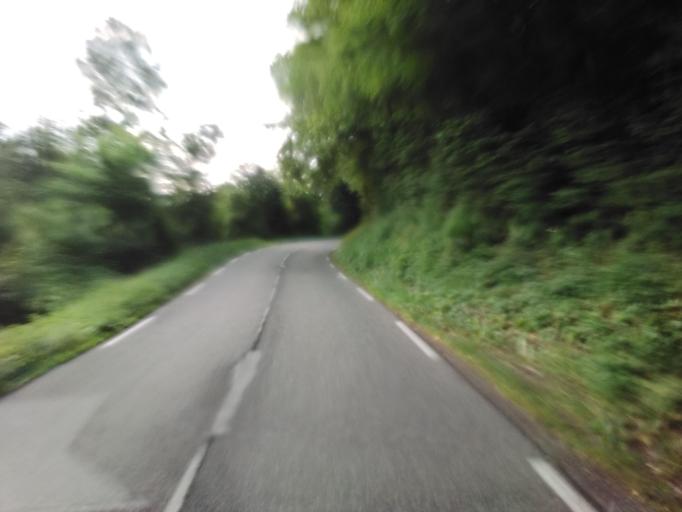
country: FR
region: Franche-Comte
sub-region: Departement du Jura
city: Arbois
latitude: 46.8970
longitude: 5.7923
